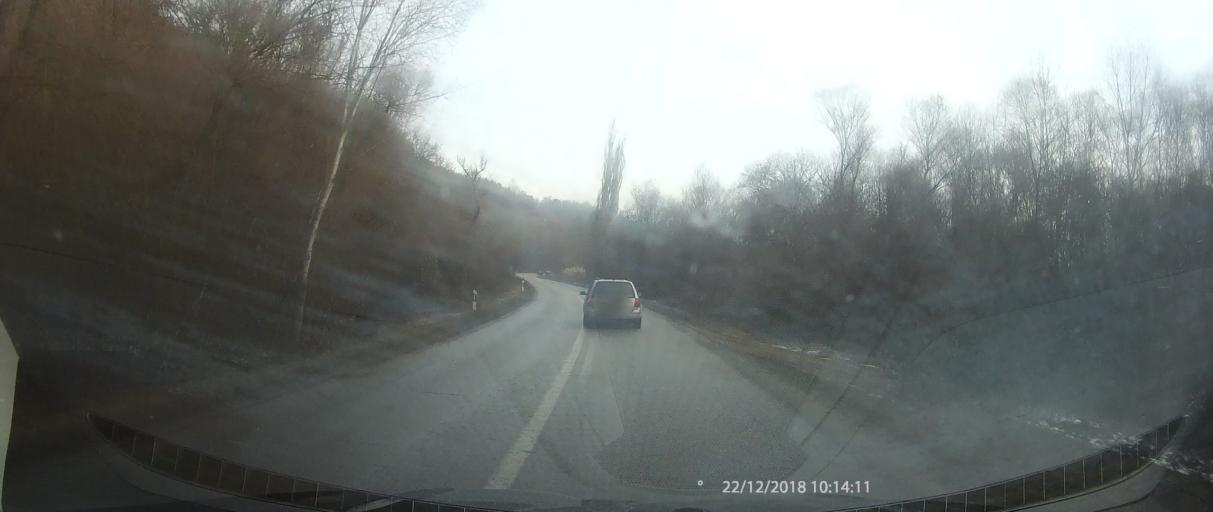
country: MK
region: Kriva Palanka
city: Kriva Palanka
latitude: 42.1742
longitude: 22.2352
